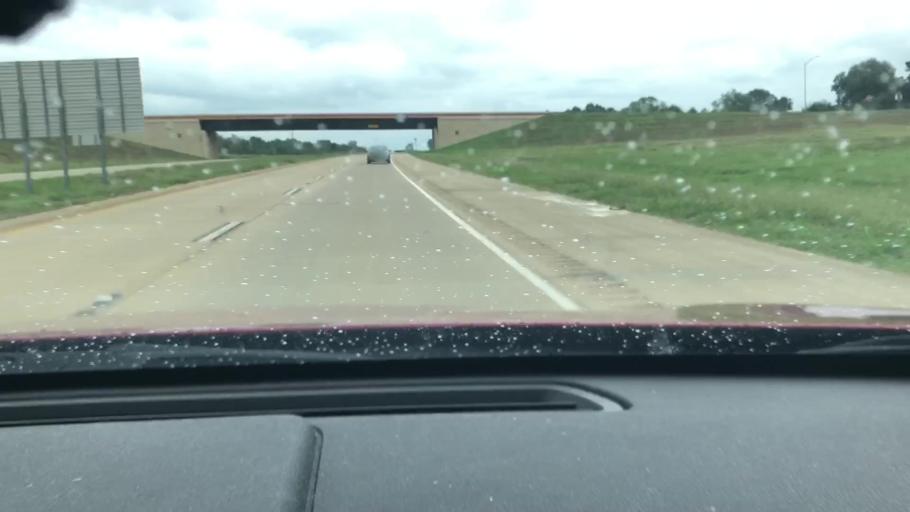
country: US
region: Texas
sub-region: Bowie County
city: Texarkana
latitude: 33.3858
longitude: -94.0450
